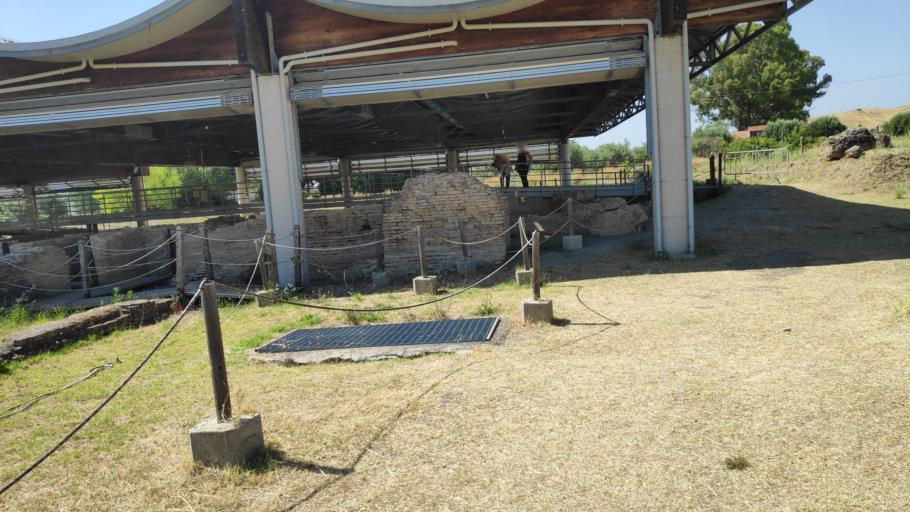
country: IT
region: Calabria
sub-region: Provincia di Reggio Calabria
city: Bianco
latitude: 38.1178
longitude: 16.1578
